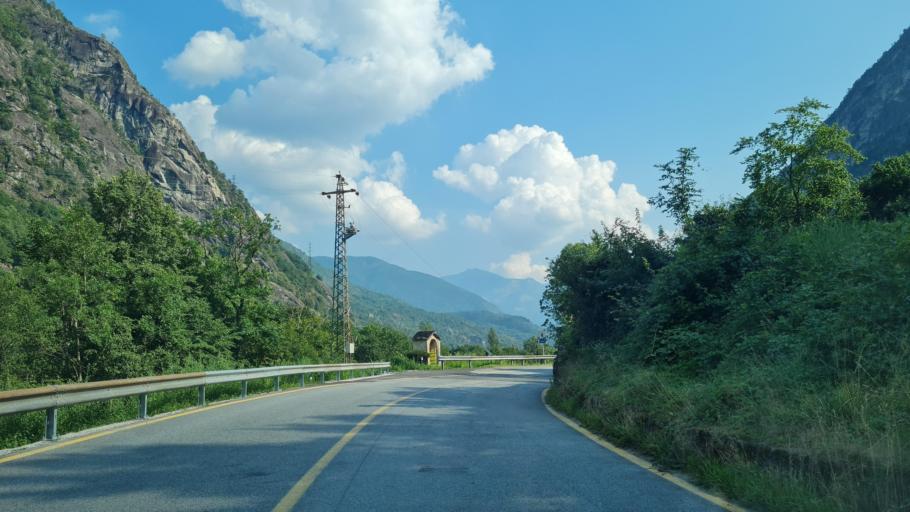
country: IT
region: Piedmont
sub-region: Provincia Verbano-Cusio-Ossola
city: Crodo
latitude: 46.1991
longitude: 8.3187
